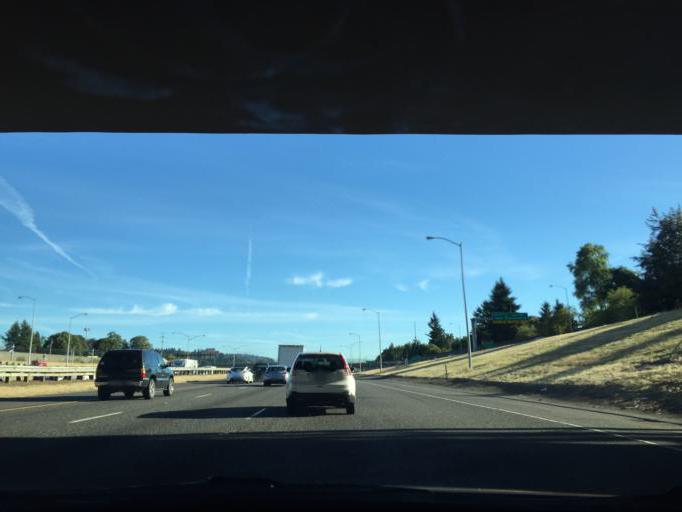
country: US
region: Oregon
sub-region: Multnomah County
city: Lents
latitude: 45.5264
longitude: -122.5656
